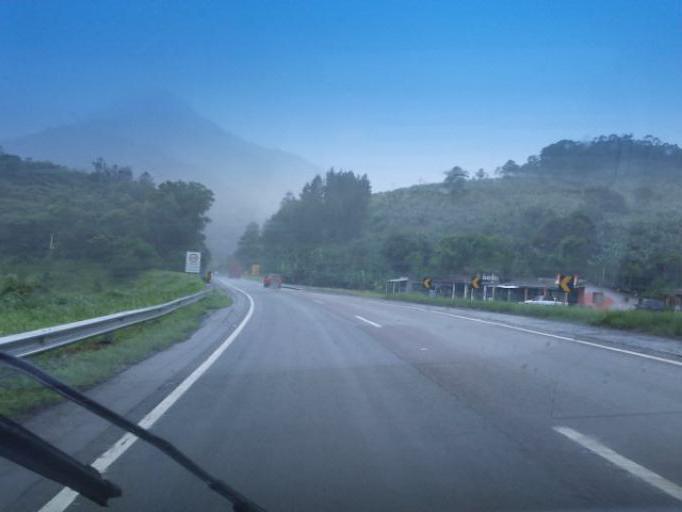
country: BR
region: Sao Paulo
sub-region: Cajati
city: Cajati
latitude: -24.8811
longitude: -48.2152
